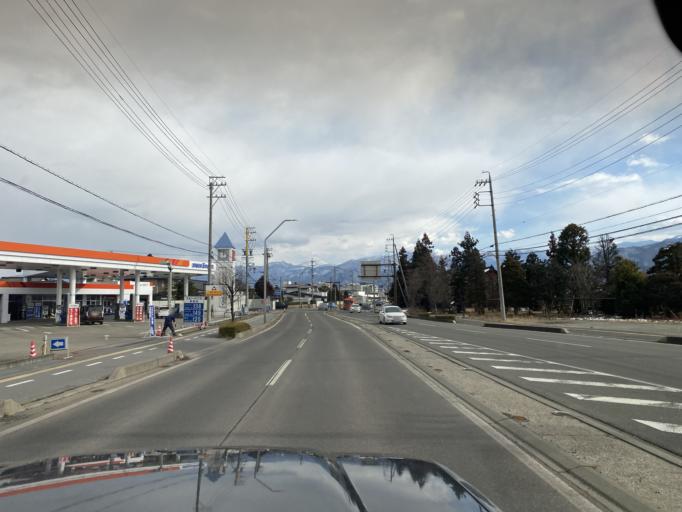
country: JP
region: Nagano
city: Nagano-shi
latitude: 36.6426
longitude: 138.2292
